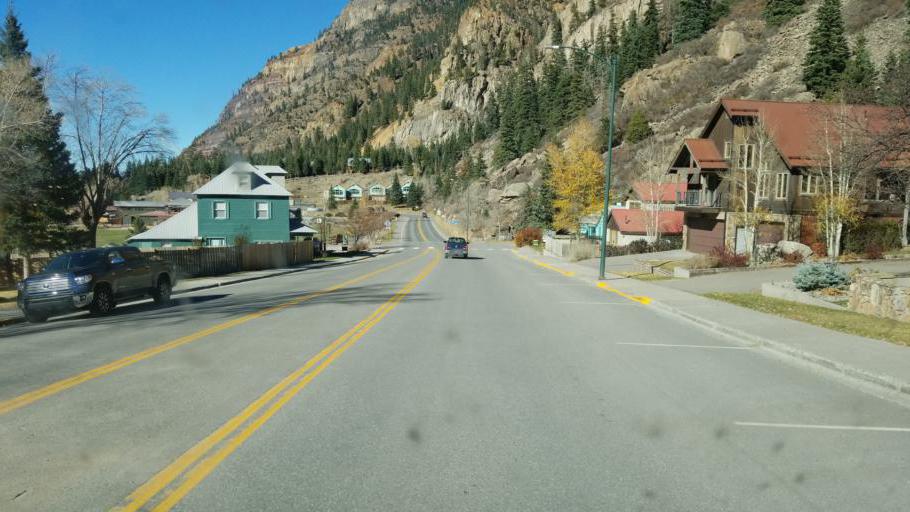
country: US
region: Colorado
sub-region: Ouray County
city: Ouray
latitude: 38.0267
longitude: -107.6714
